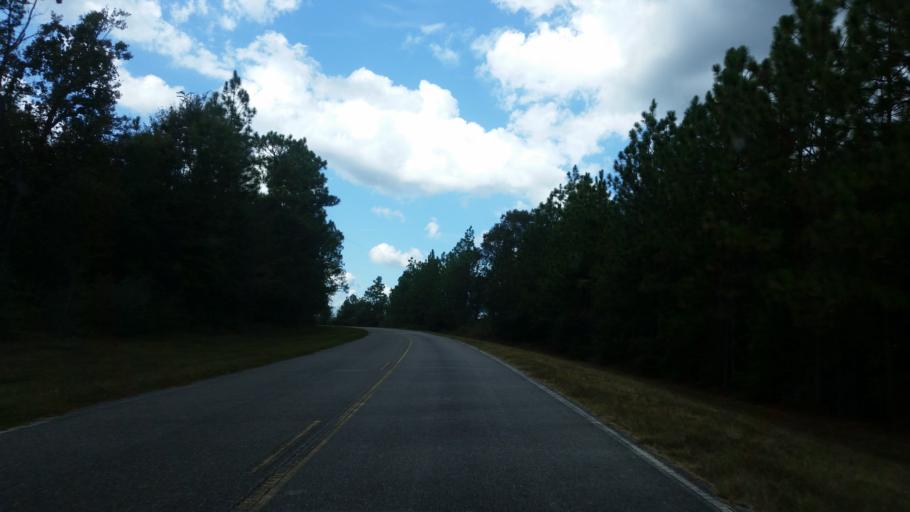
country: US
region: Alabama
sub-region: Escambia County
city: Atmore
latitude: 30.8959
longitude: -87.5502
